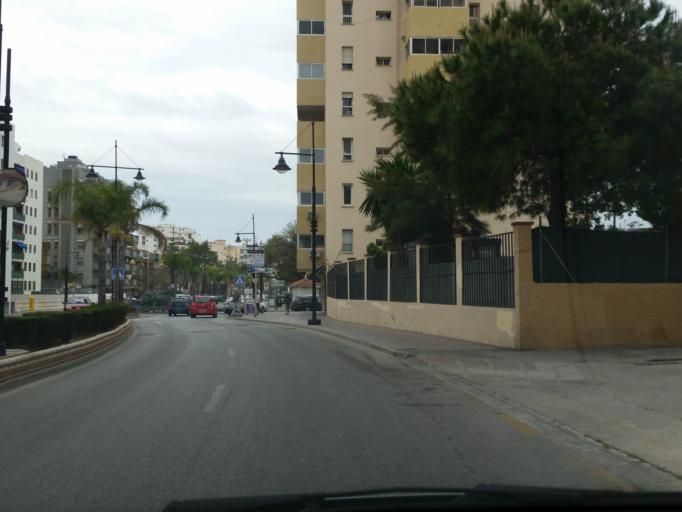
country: ES
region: Andalusia
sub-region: Provincia de Malaga
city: Fuengirola
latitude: 36.5456
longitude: -4.6212
